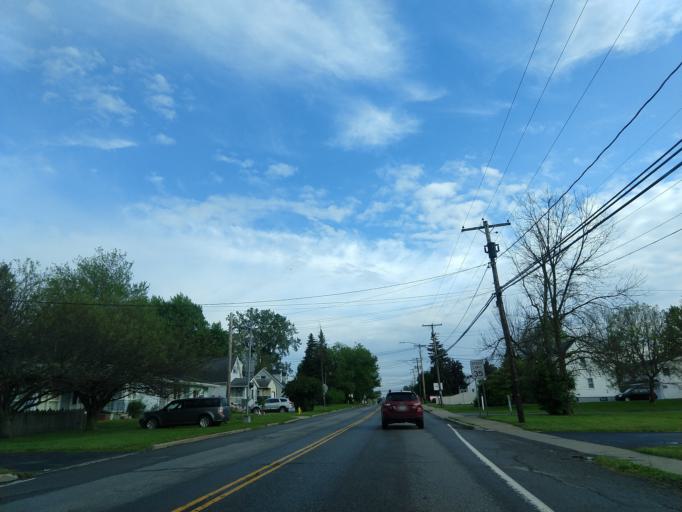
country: US
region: New York
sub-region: Erie County
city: West Seneca
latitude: 42.8592
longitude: -78.7876
